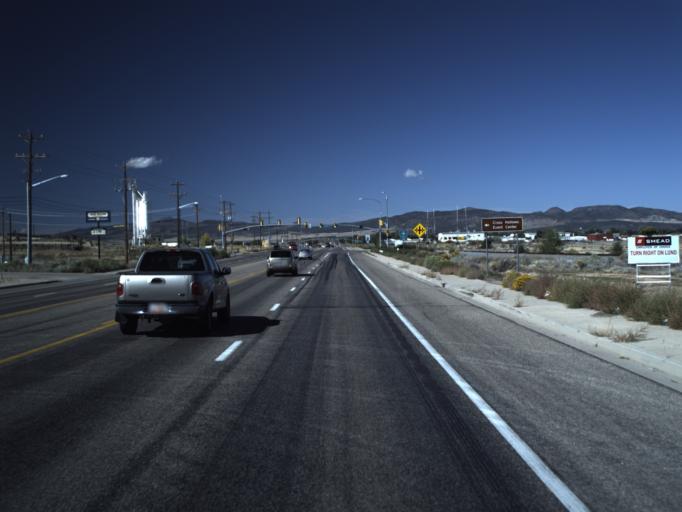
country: US
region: Utah
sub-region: Iron County
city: Cedar City
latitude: 37.6851
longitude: -113.1041
